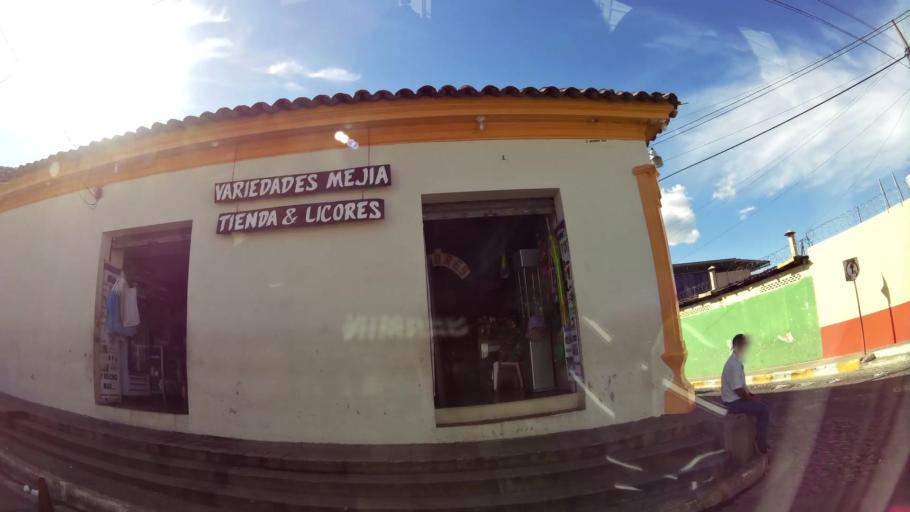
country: SV
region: Cuscatlan
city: Suchitoto
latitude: 13.9363
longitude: -89.0271
